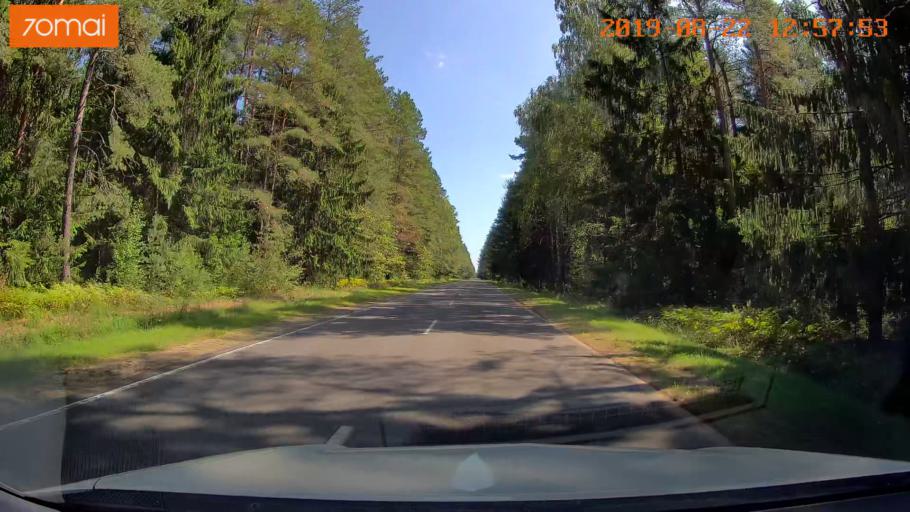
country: BY
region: Minsk
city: Prawdzinski
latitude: 53.4269
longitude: 27.7581
